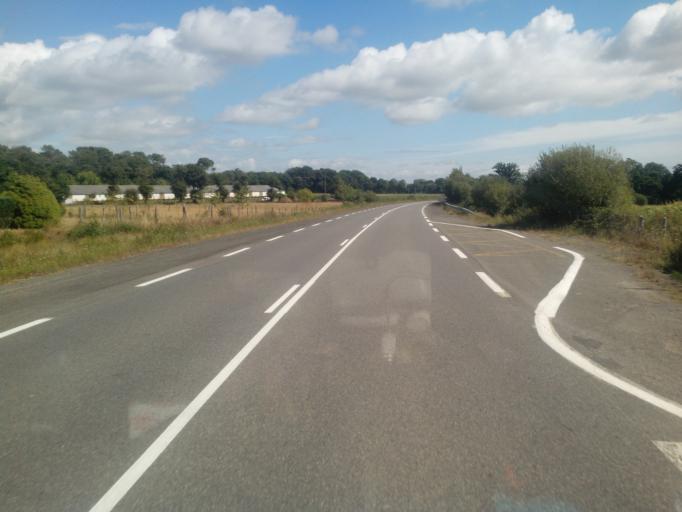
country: FR
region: Brittany
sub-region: Departement du Morbihan
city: Limerzel
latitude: 47.6126
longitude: -2.3925
